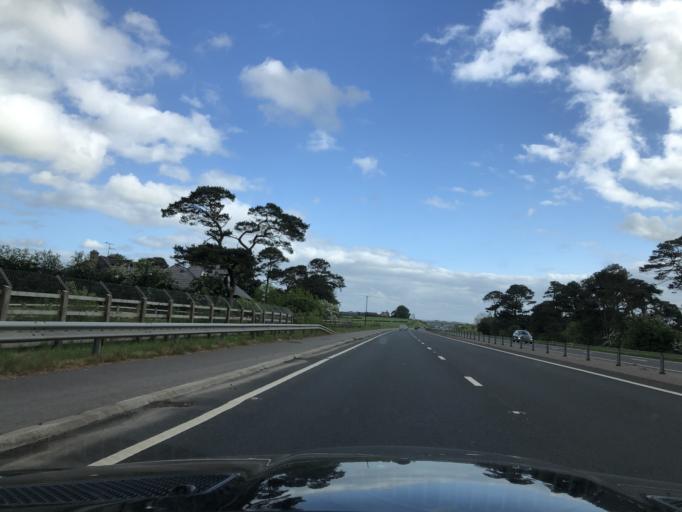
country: GB
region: Northern Ireland
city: Dunloy
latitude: 54.9730
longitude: -6.3438
